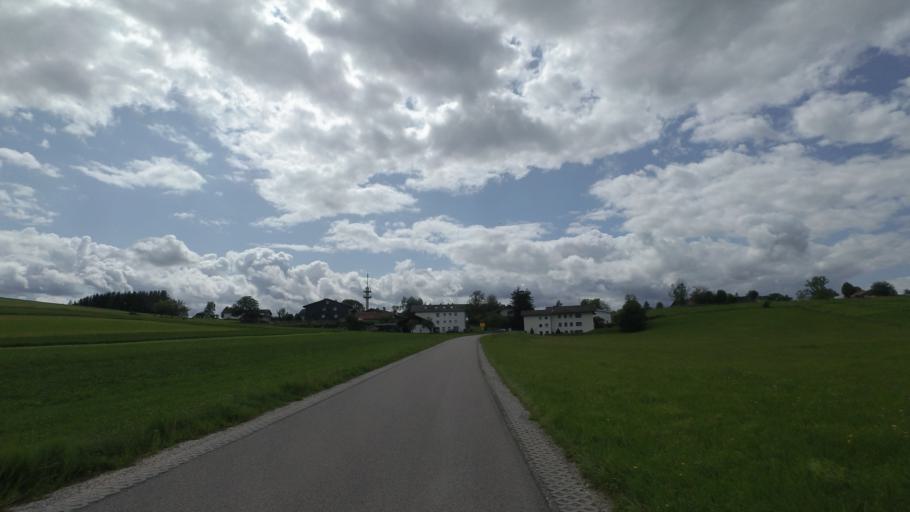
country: DE
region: Bavaria
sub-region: Upper Bavaria
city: Vachendorf
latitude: 47.8638
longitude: 12.6123
